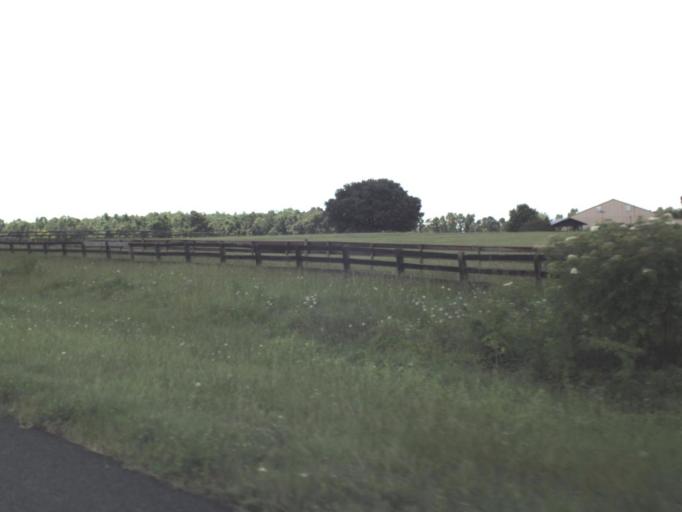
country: US
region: Florida
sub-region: Jefferson County
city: Monticello
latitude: 30.3175
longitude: -83.7612
